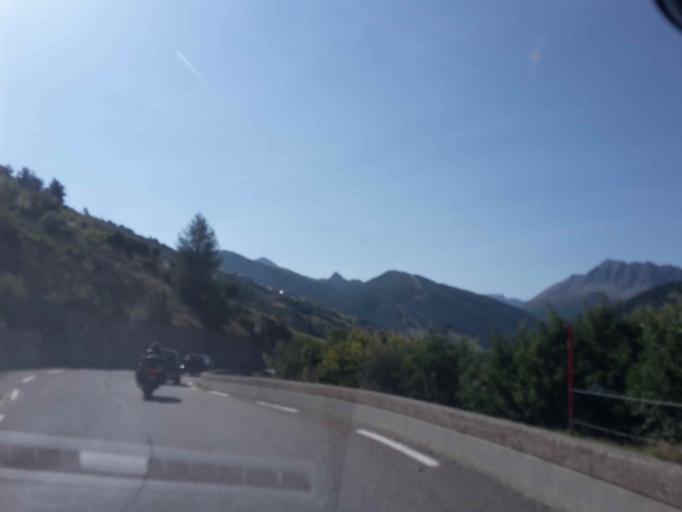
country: FR
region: Provence-Alpes-Cote d'Azur
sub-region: Departement des Hautes-Alpes
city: Guillestre
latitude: 44.6163
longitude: 6.6854
